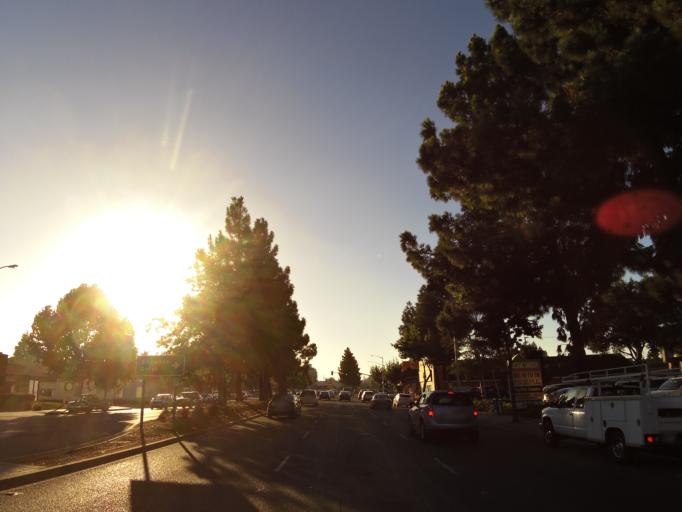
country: US
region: California
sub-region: Santa Clara County
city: Los Altos
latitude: 37.3987
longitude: -122.1086
